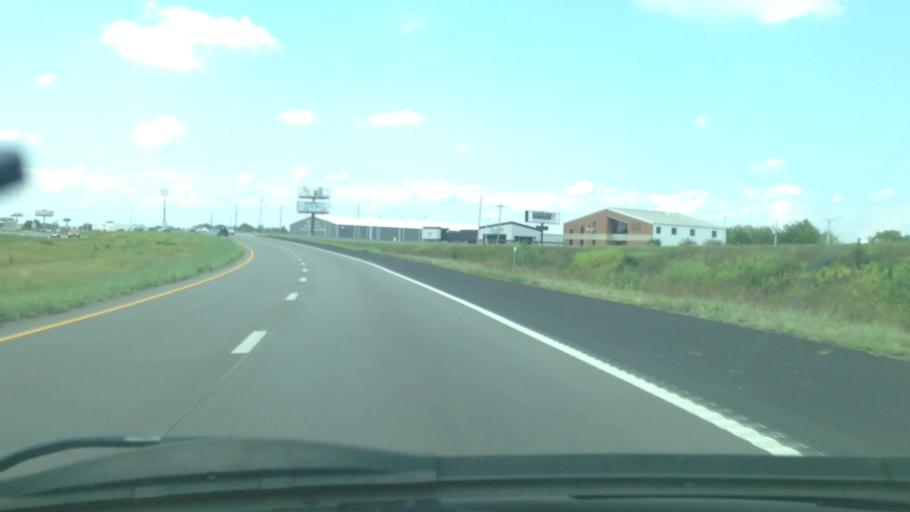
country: US
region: Missouri
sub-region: Lincoln County
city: Moscow Mills
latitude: 38.9475
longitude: -90.9288
